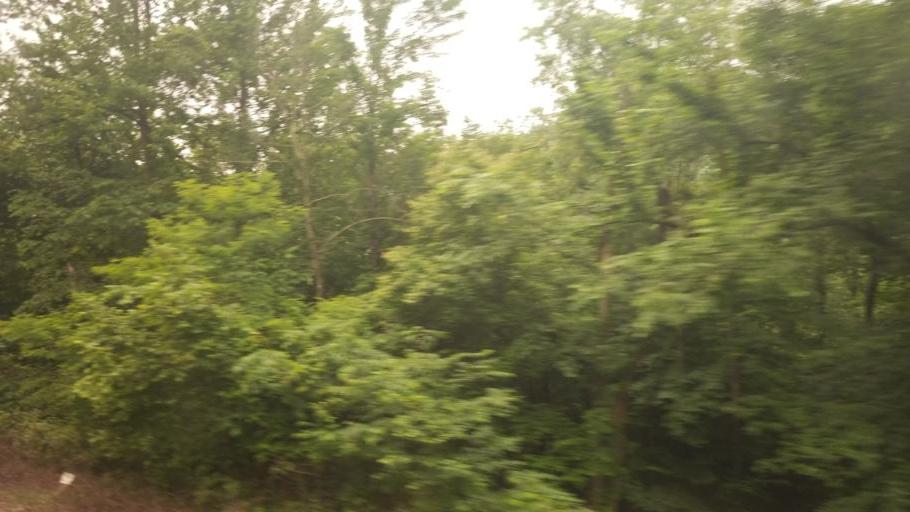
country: US
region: Maryland
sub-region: Allegany County
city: Cumberland
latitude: 39.8297
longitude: -78.7525
